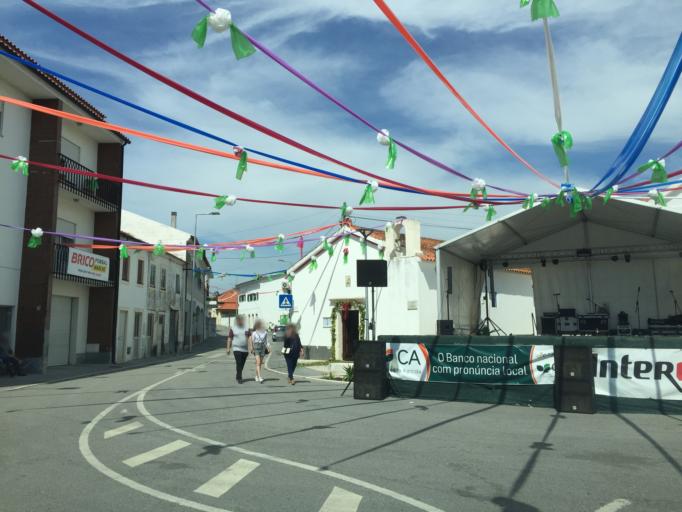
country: PT
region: Coimbra
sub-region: Soure
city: Soure
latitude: 40.0042
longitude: -8.5821
